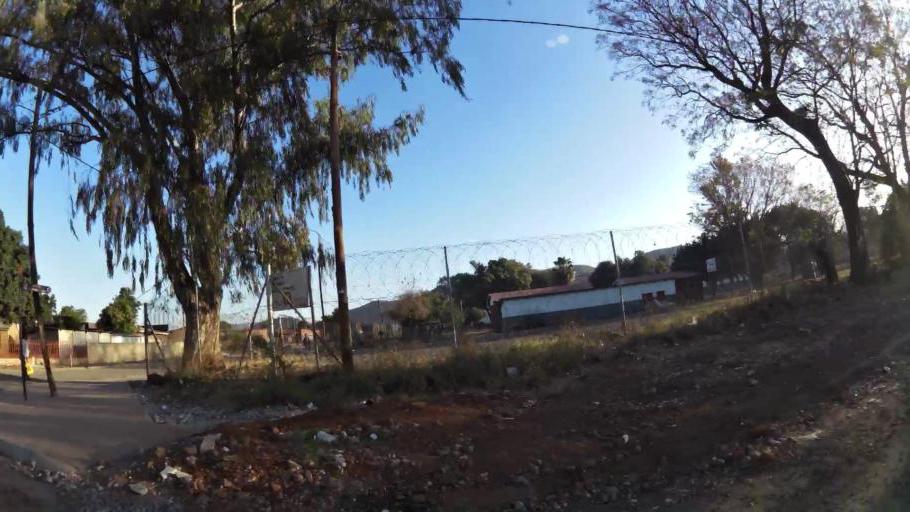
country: ZA
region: North-West
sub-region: Bojanala Platinum District Municipality
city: Rustenburg
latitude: -25.6347
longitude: 27.2084
